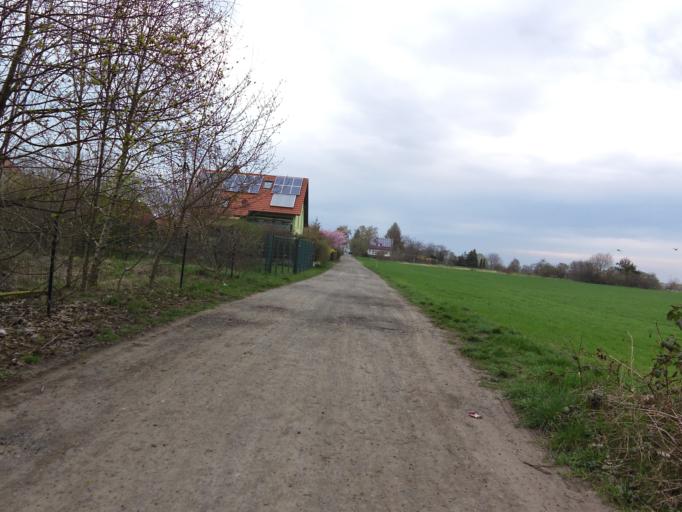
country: DE
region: Thuringia
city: Gotha
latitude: 50.9593
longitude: 10.6964
